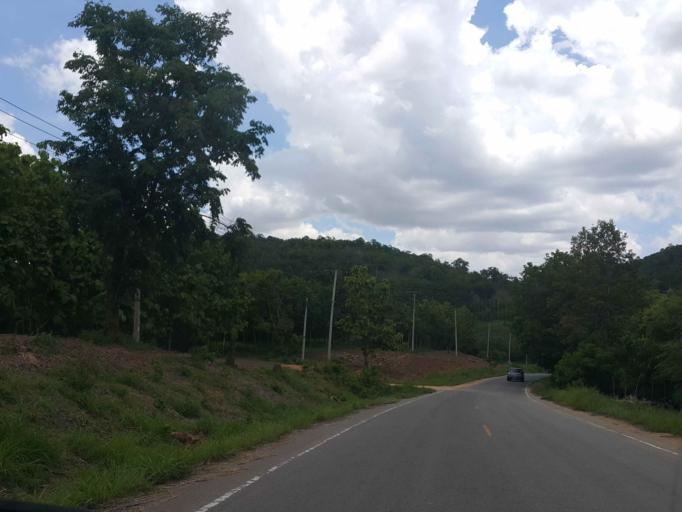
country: TH
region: Nan
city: Wiang Sa
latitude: 18.5398
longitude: 100.5474
